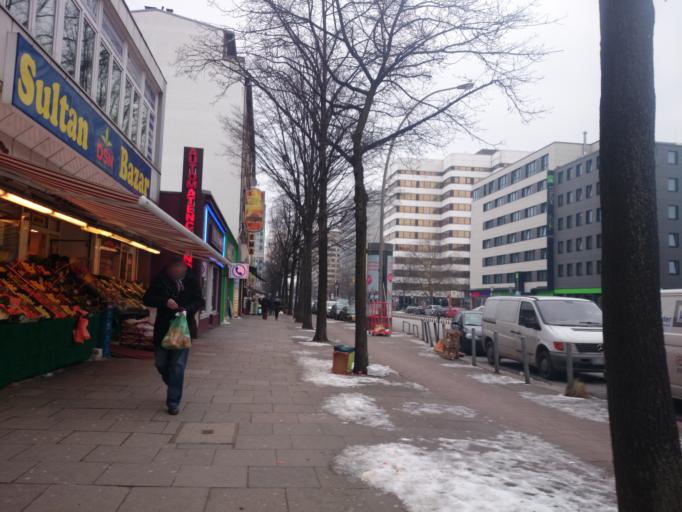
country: DE
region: Hamburg
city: St. Georg
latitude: 53.5544
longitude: 10.0140
